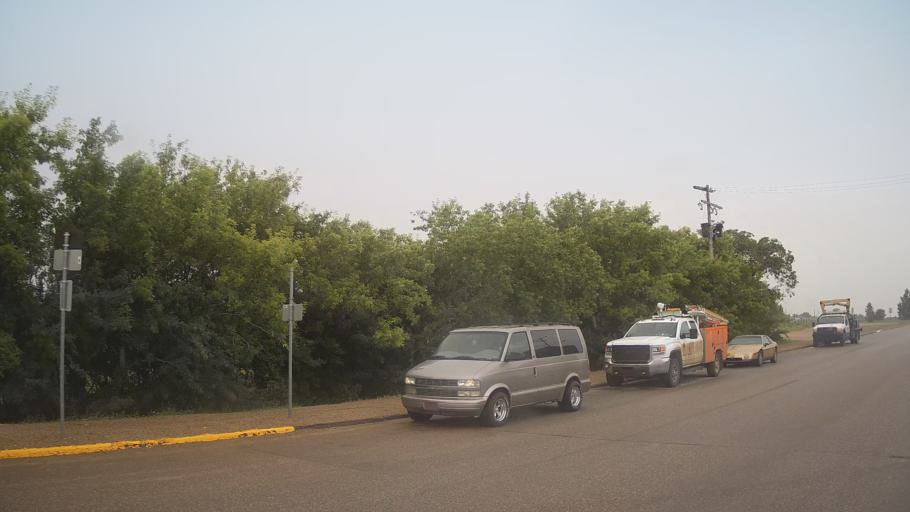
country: CA
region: Saskatchewan
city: Biggar
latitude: 52.0540
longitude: -107.9866
